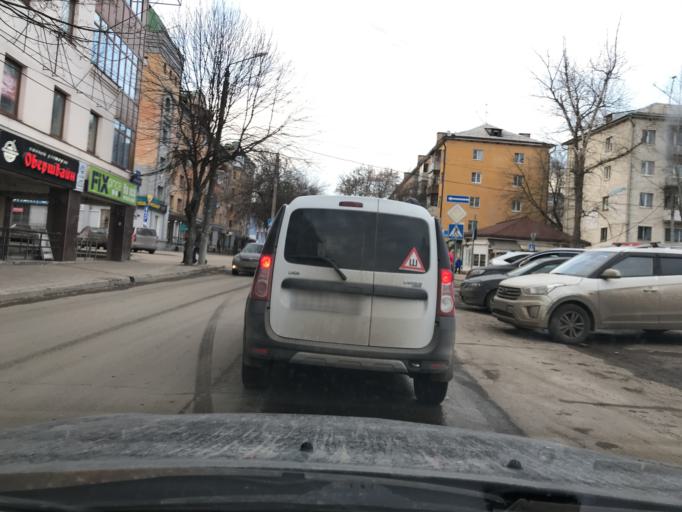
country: RU
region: Kaluga
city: Kaluga
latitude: 54.5133
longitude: 36.2468
